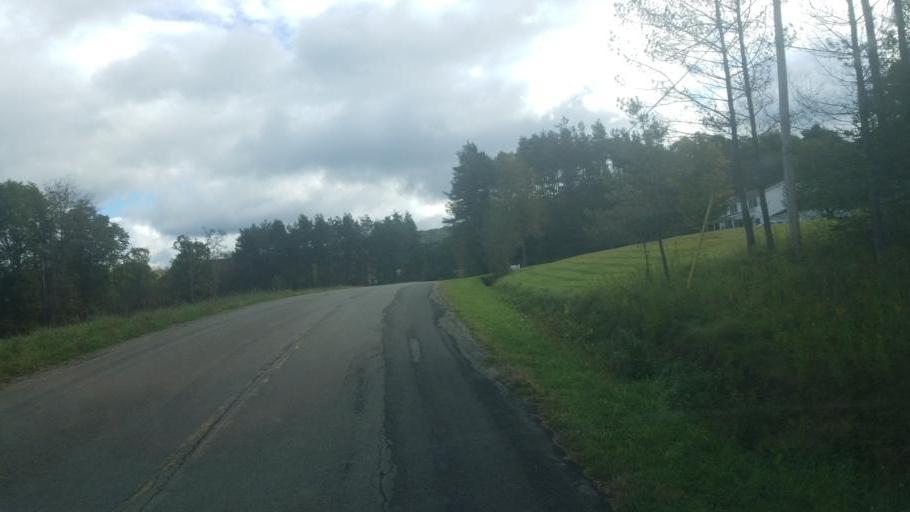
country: US
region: New York
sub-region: Cattaraugus County
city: Weston Mills
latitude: 42.1136
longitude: -78.3251
